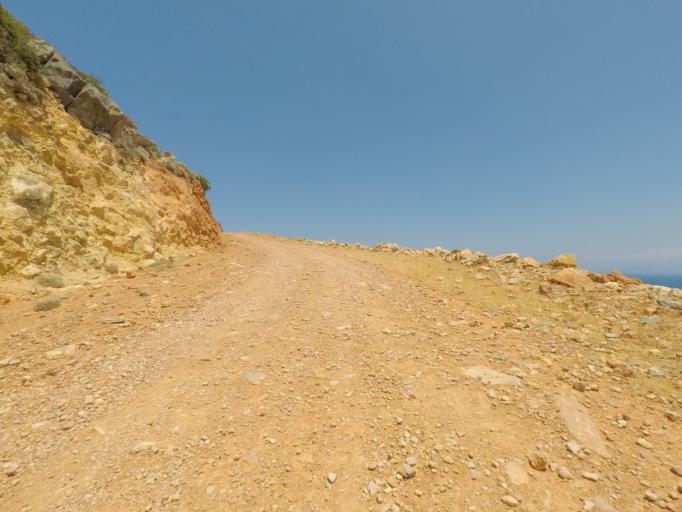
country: GR
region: Crete
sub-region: Nomos Lasithiou
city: Elounda
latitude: 35.3185
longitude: 25.7546
